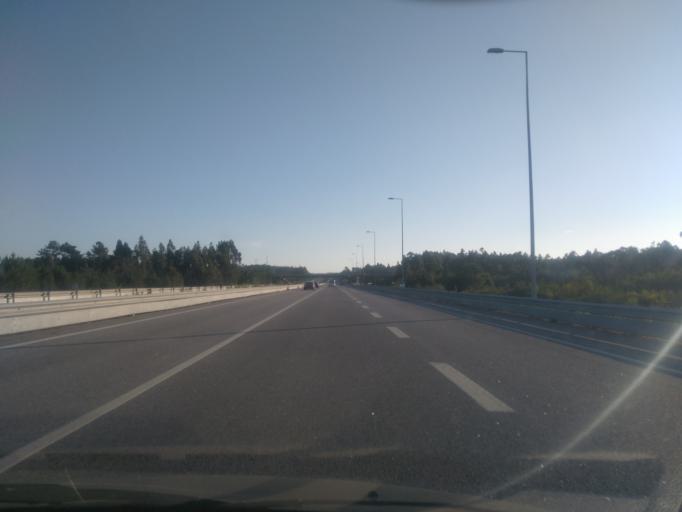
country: PT
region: Coimbra
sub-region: Figueira da Foz
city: Alhadas
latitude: 40.2244
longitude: -8.7956
